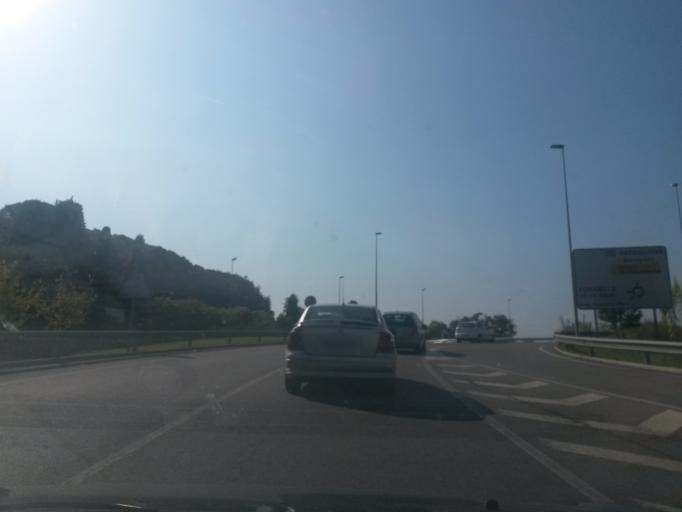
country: ES
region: Catalonia
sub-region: Provincia de Girona
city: Fornells de la Selva
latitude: 41.9433
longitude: 2.8063
